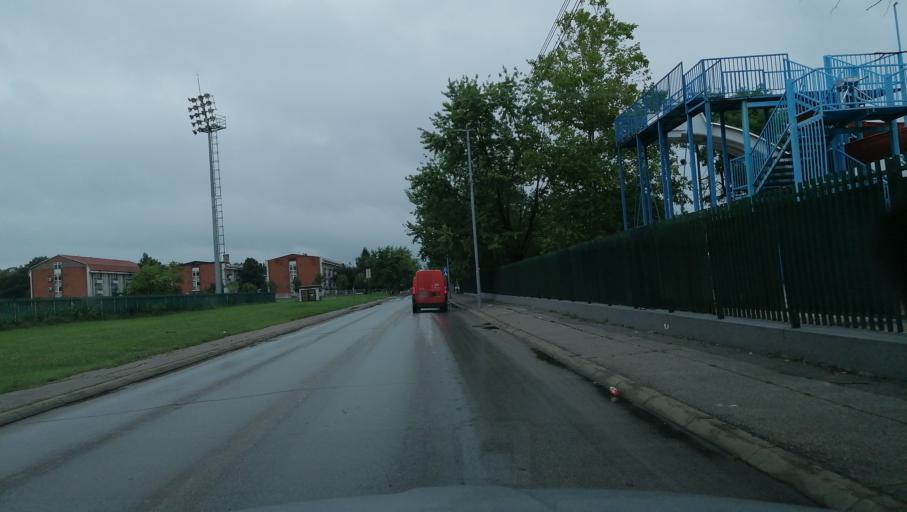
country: RS
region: Central Serbia
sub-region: Rasinski Okrug
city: Krusevac
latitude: 43.5737
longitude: 21.3284
